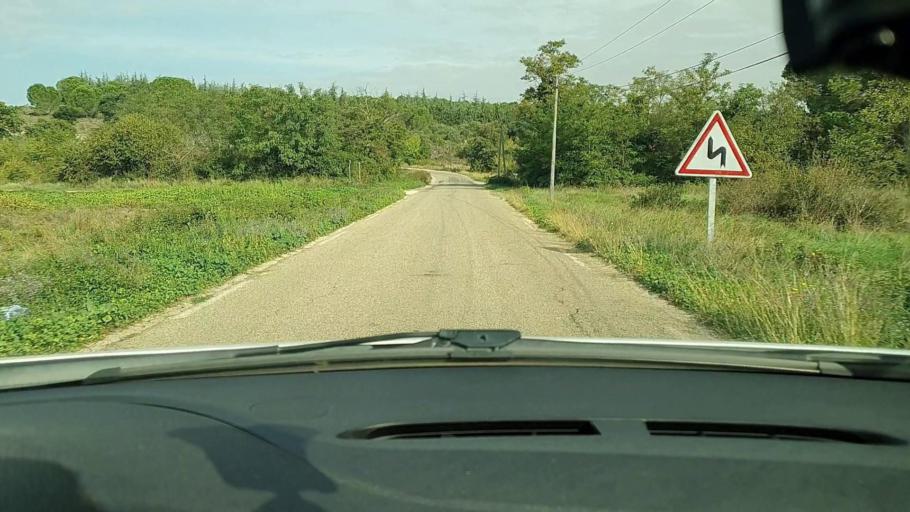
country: FR
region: Languedoc-Roussillon
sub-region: Departement du Gard
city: Saint-Quentin-la-Poterie
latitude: 44.1156
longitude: 4.4149
